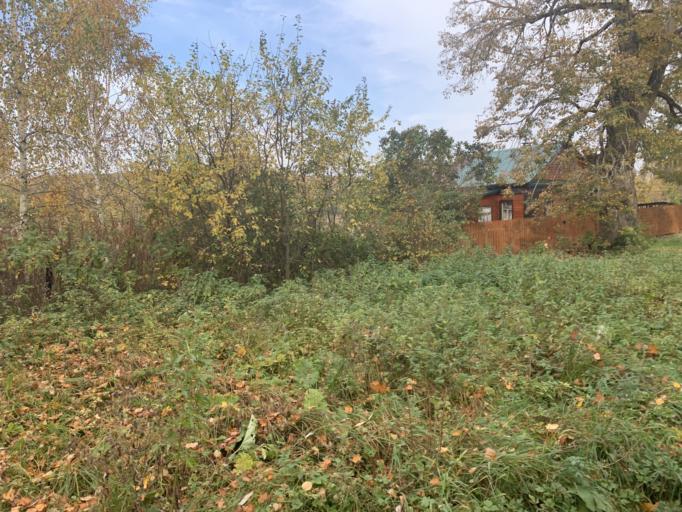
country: RU
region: Jaroslavl
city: Porech'ye-Rybnoye
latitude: 56.9803
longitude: 39.3836
